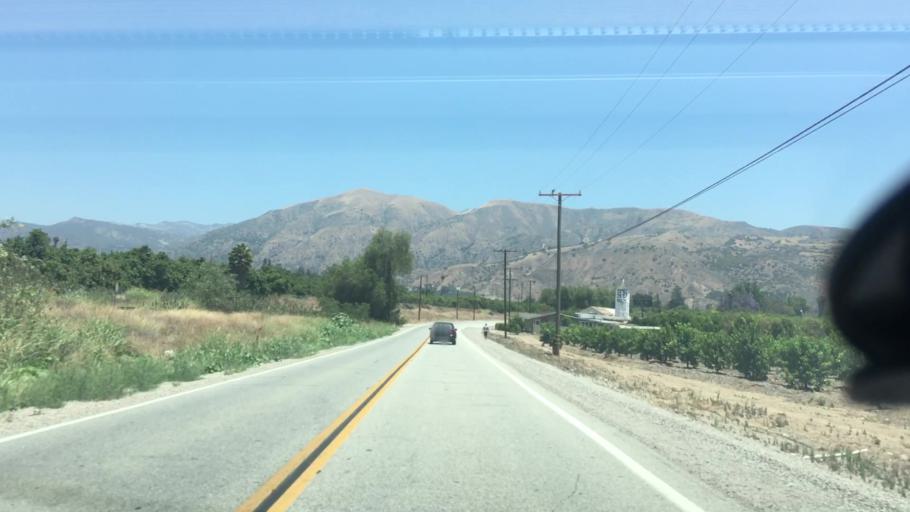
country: US
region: California
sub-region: Ventura County
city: Fillmore
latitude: 34.4062
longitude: -118.9437
